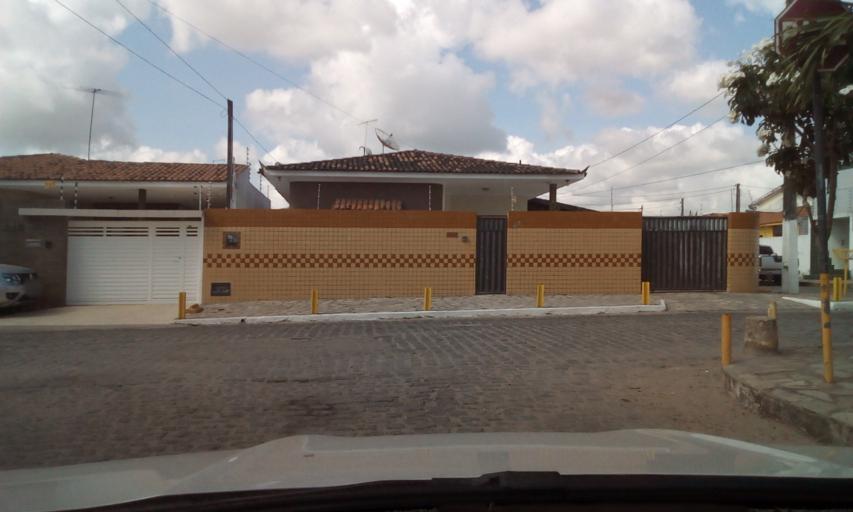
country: BR
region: Paraiba
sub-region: Joao Pessoa
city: Joao Pessoa
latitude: -7.1763
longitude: -34.8580
